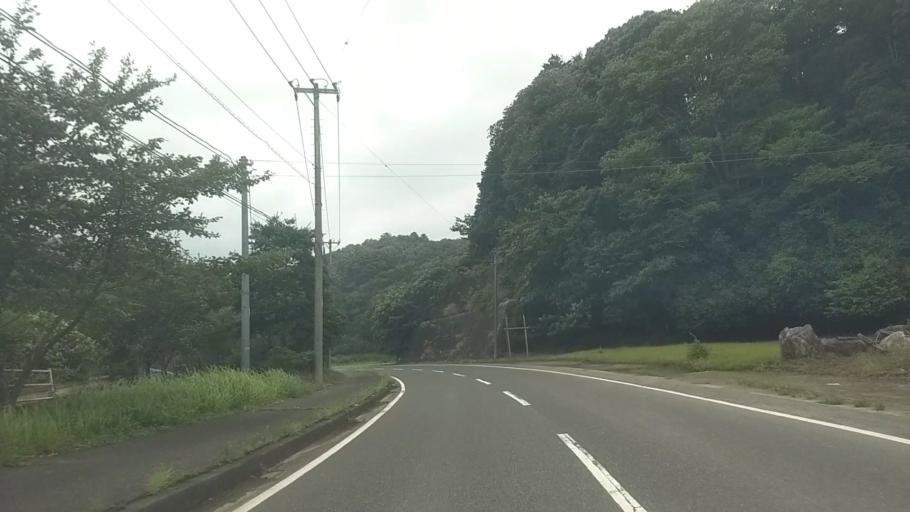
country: JP
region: Chiba
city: Kawaguchi
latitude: 35.2483
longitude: 140.0390
